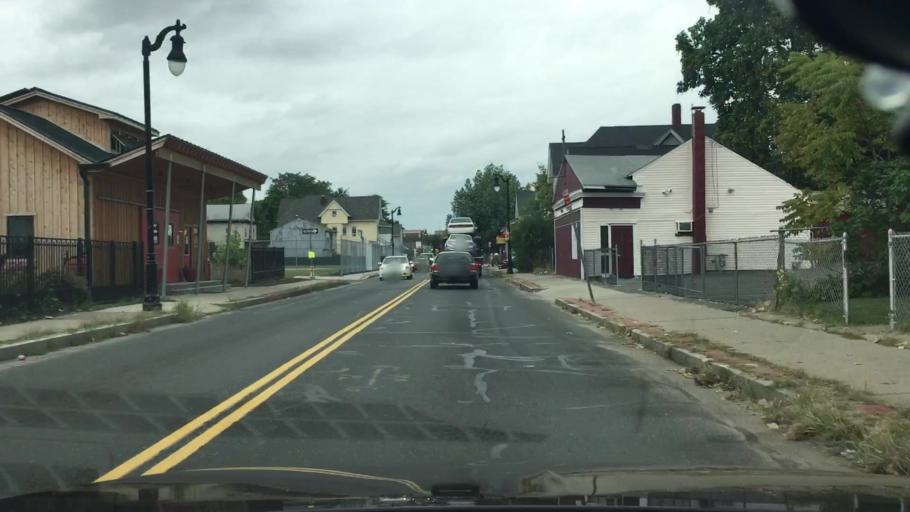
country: US
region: Massachusetts
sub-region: Hampden County
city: Springfield
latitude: 42.1037
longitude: -72.5707
